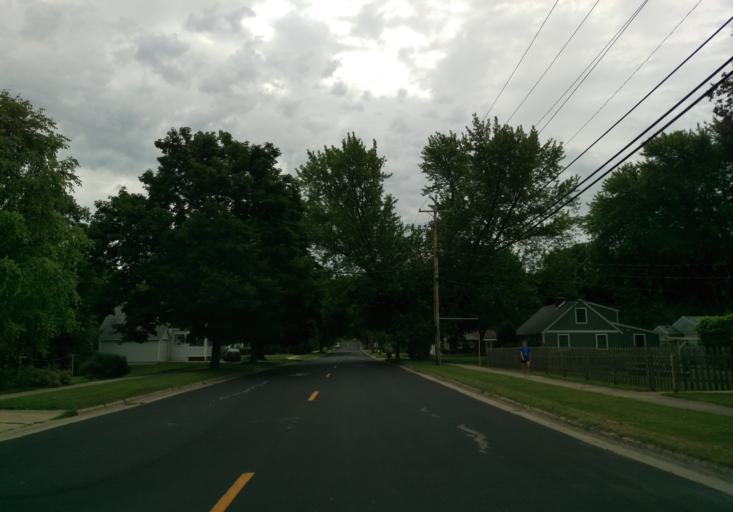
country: US
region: Wisconsin
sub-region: Dane County
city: Shorewood Hills
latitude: 43.0681
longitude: -89.4499
